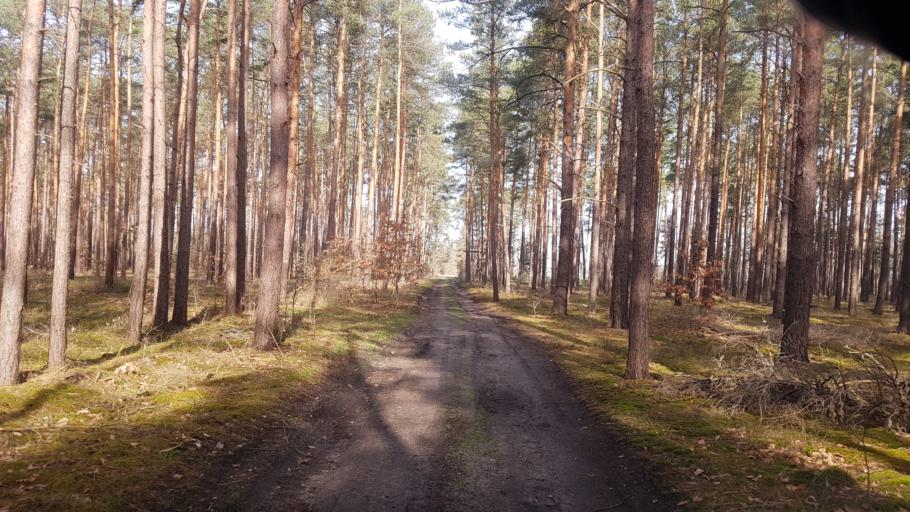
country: DE
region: Brandenburg
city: Schonborn
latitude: 51.6829
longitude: 13.4866
